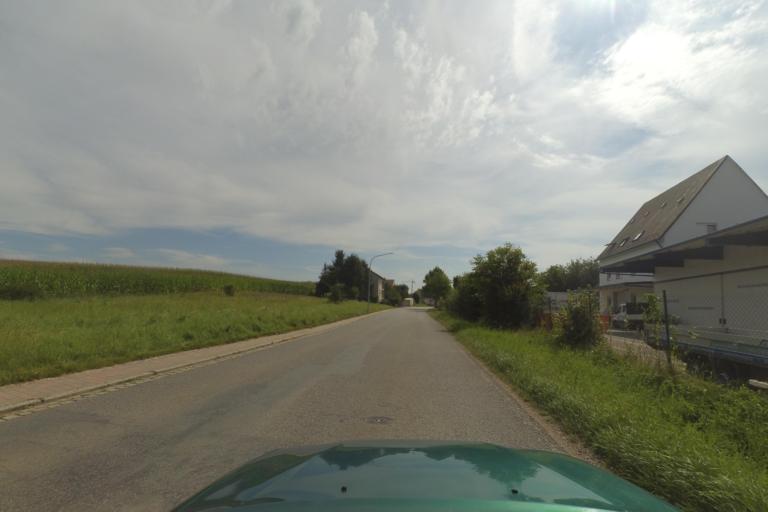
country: DE
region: Bavaria
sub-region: Upper Palatinate
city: Thalmassing
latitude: 48.9323
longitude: 12.1229
